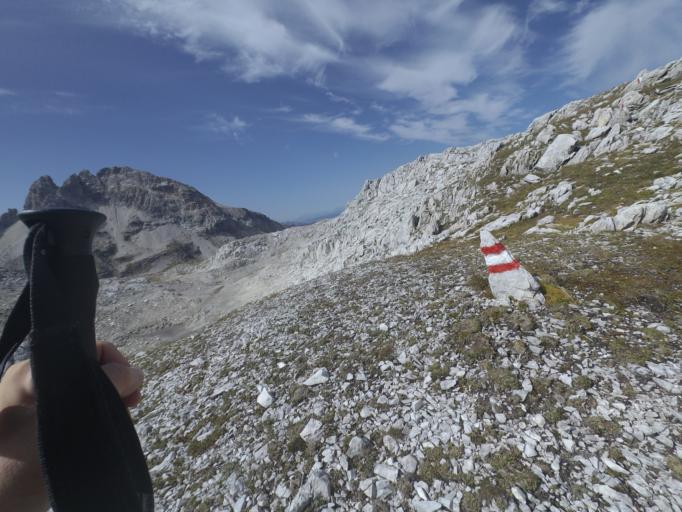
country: AT
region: Salzburg
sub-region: Politischer Bezirk Sankt Johann im Pongau
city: Kleinarl
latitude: 47.2162
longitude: 13.3905
